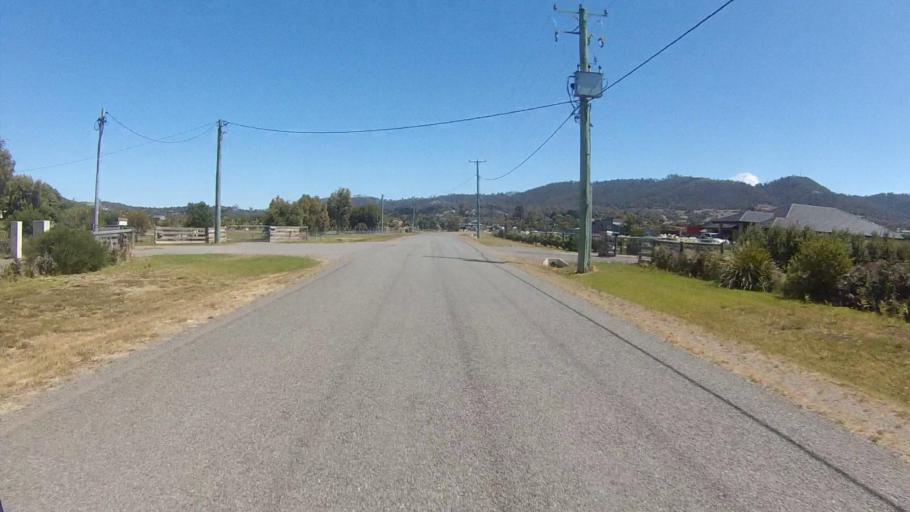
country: AU
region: Tasmania
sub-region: Clarence
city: Seven Mile Beach
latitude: -42.8513
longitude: 147.4917
